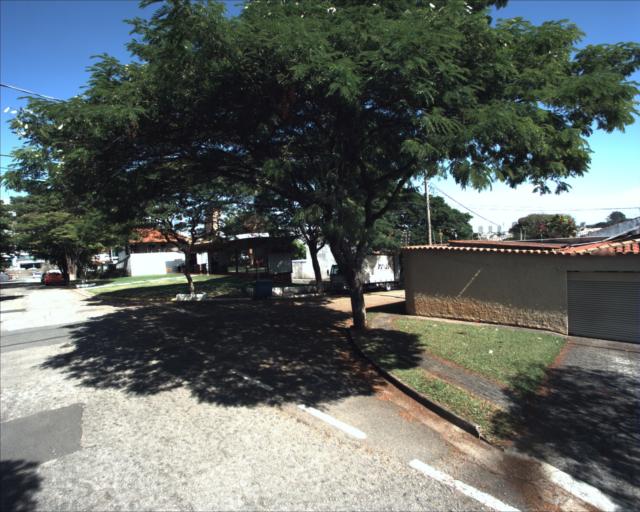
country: BR
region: Sao Paulo
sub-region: Sorocaba
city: Sorocaba
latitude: -23.5280
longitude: -47.4670
